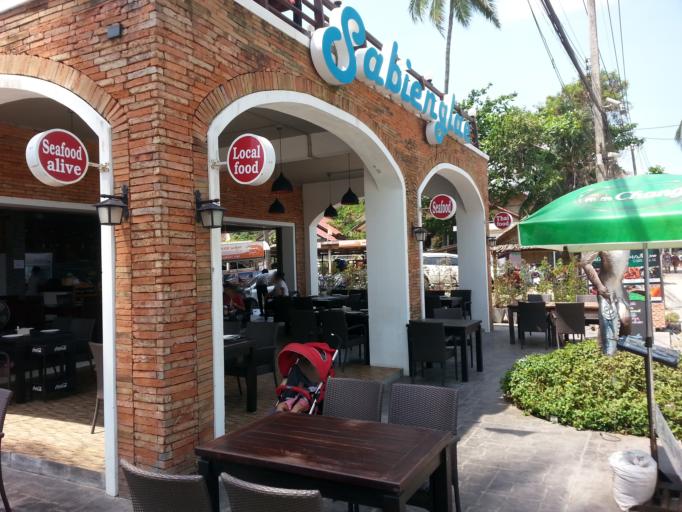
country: TH
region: Surat Thani
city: Ko Samui
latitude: 9.5602
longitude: 100.0271
